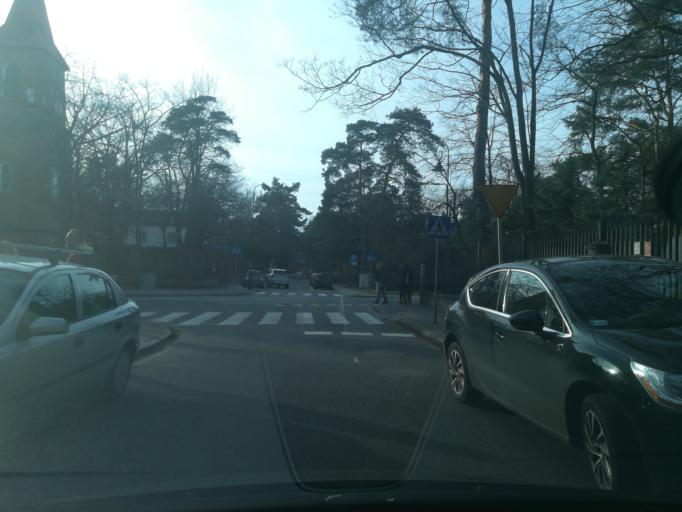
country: PL
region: Masovian Voivodeship
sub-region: Powiat piaseczynski
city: Konstancin-Jeziorna
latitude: 52.0825
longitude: 21.1197
